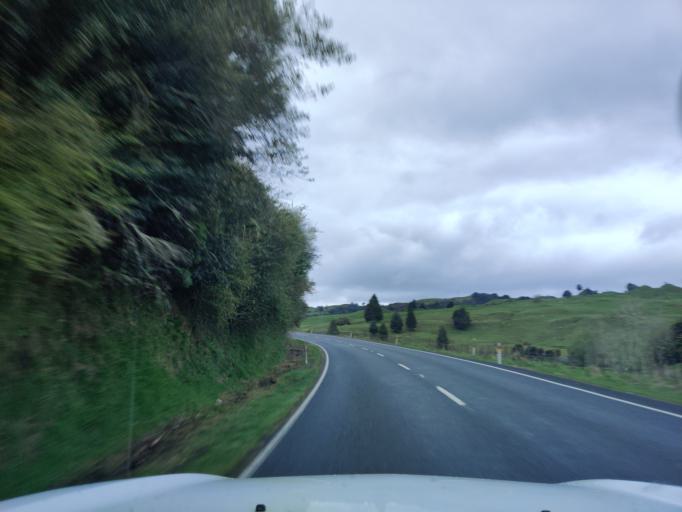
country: NZ
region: Waikato
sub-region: Otorohanga District
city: Otorohanga
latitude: -38.5945
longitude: 175.2193
